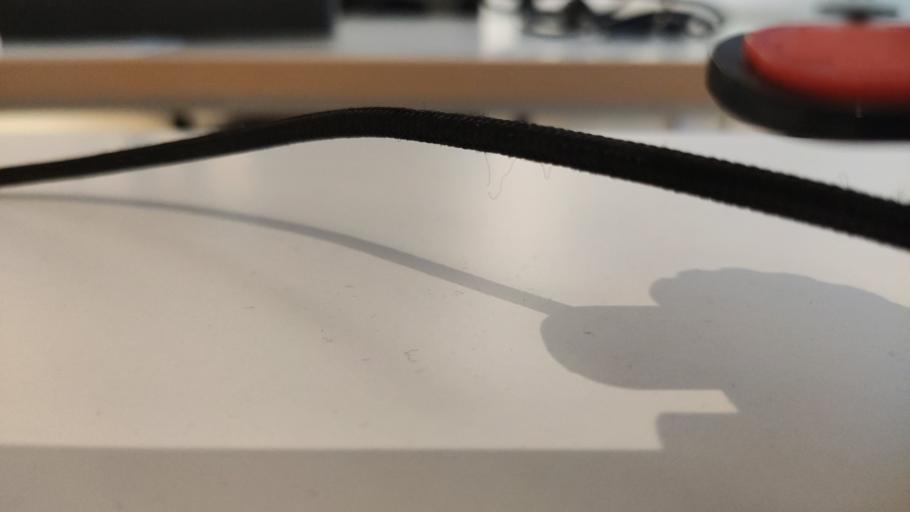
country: RU
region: Moskovskaya
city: Ruza
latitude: 55.7824
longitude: 36.2740
